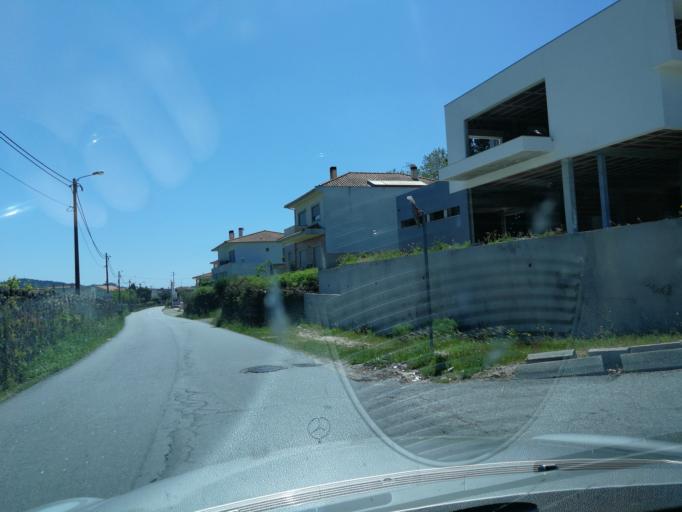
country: PT
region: Viana do Castelo
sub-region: Viana do Castelo
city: Meadela
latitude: 41.7177
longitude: -8.7986
